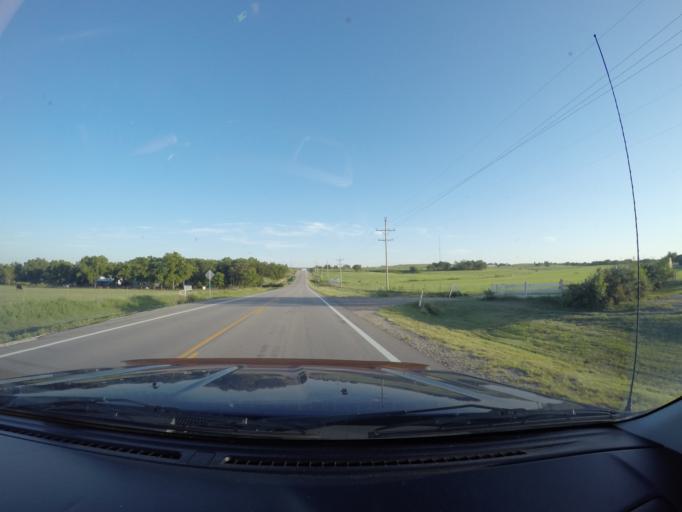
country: US
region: Kansas
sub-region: Wabaunsee County
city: Alma
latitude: 39.0716
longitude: -96.2891
